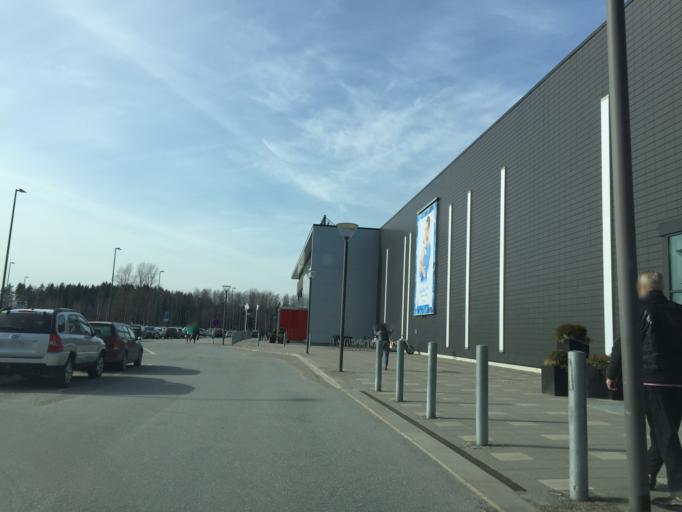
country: SE
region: OErebro
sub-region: Orebro Kommun
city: Orebro
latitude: 59.2165
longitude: 15.1390
